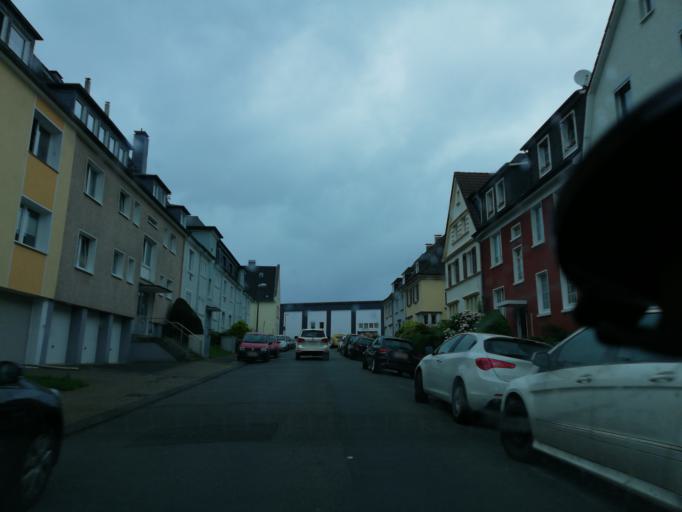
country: DE
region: North Rhine-Westphalia
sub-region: Regierungsbezirk Dusseldorf
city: Solingen
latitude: 51.2362
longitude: 7.0835
